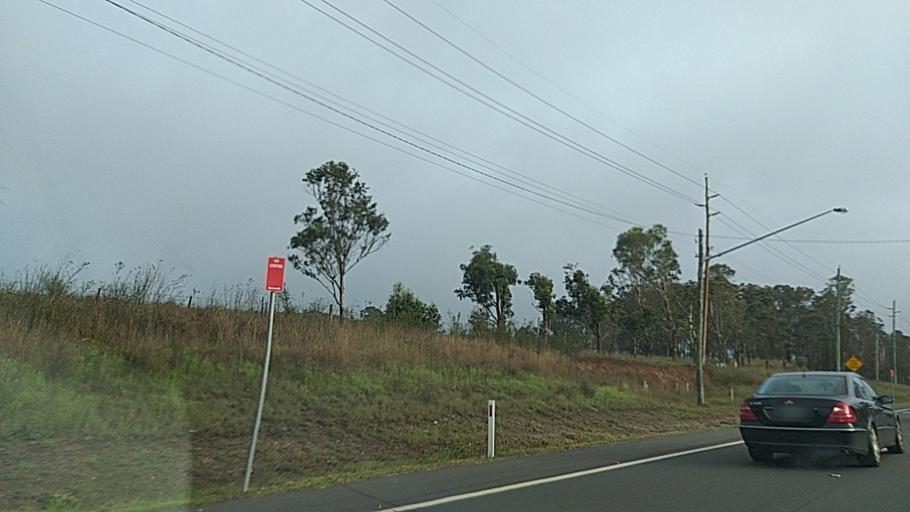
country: AU
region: New South Wales
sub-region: Penrith Municipality
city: Glenmore Park
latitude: -33.8045
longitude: 150.6964
